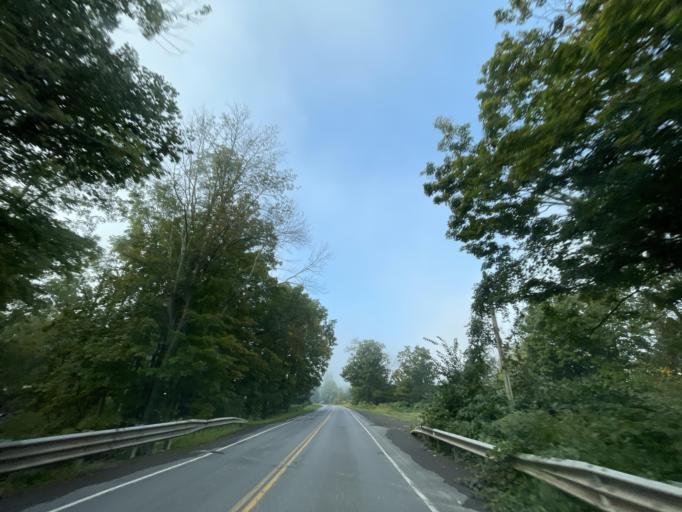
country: US
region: New York
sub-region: Chenango County
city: Oxford
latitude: 42.3755
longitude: -75.6330
